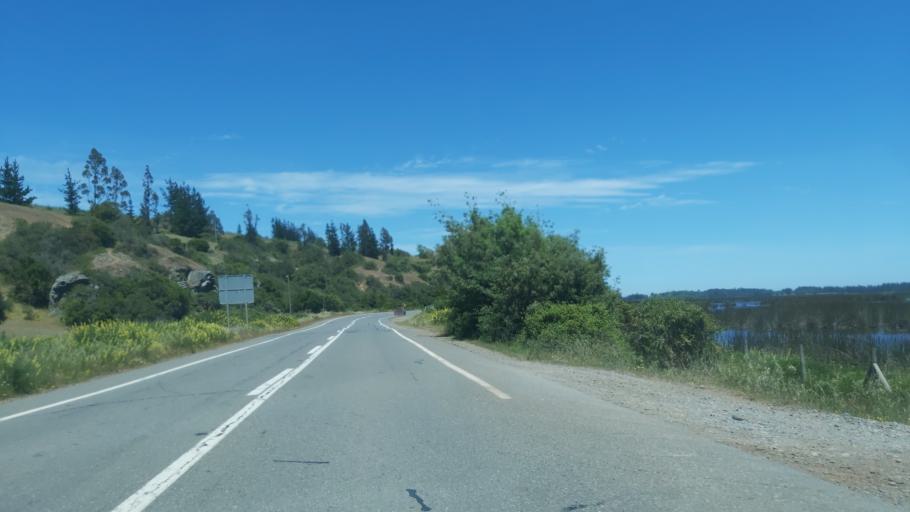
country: CL
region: Maule
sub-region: Provincia de Talca
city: Constitucion
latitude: -35.1556
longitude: -72.2463
